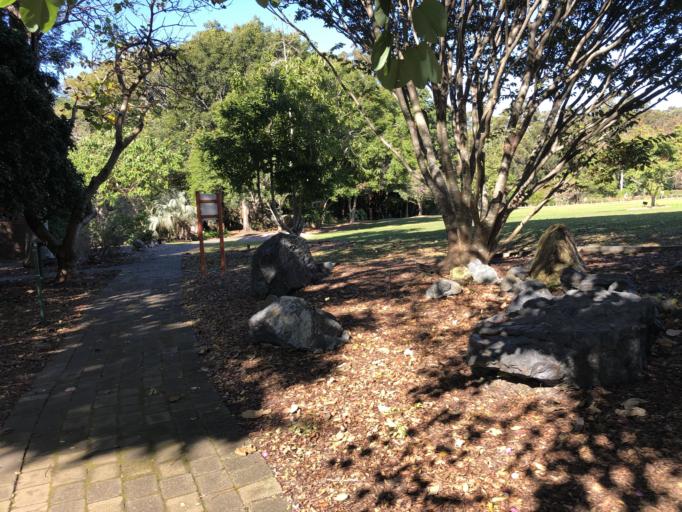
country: AU
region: New South Wales
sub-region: Coffs Harbour
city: Coffs Harbour
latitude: -30.2928
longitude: 153.1254
